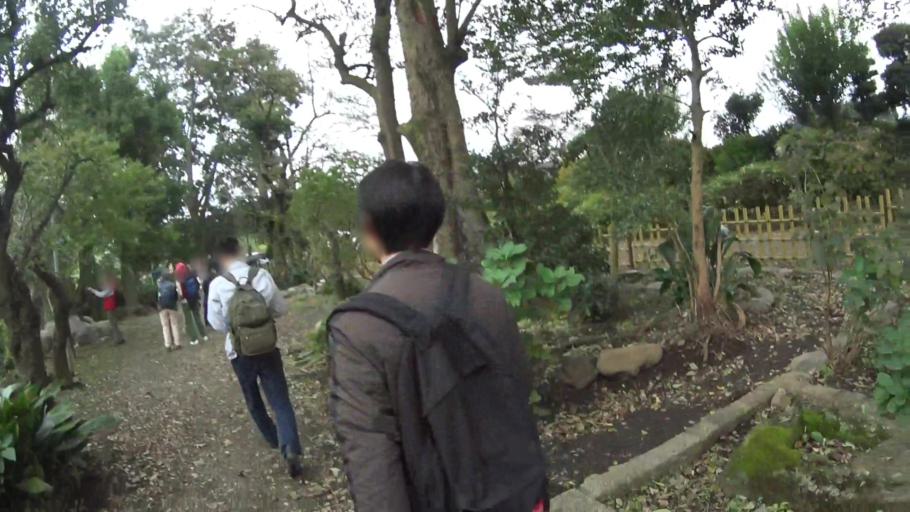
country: JP
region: Kanagawa
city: Hadano
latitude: 35.3943
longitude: 139.2239
